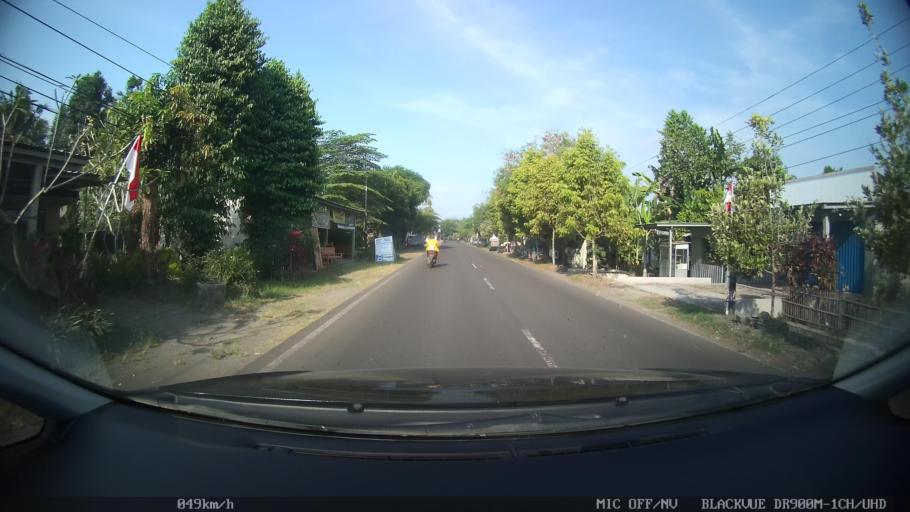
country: ID
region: Daerah Istimewa Yogyakarta
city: Pandak
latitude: -7.9018
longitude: 110.3016
